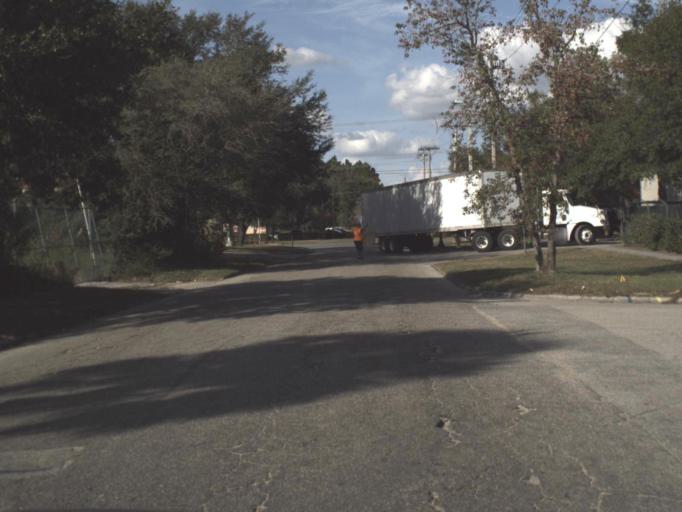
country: US
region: Florida
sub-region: Seminole County
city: Sanford
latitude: 28.8106
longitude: -81.2889
